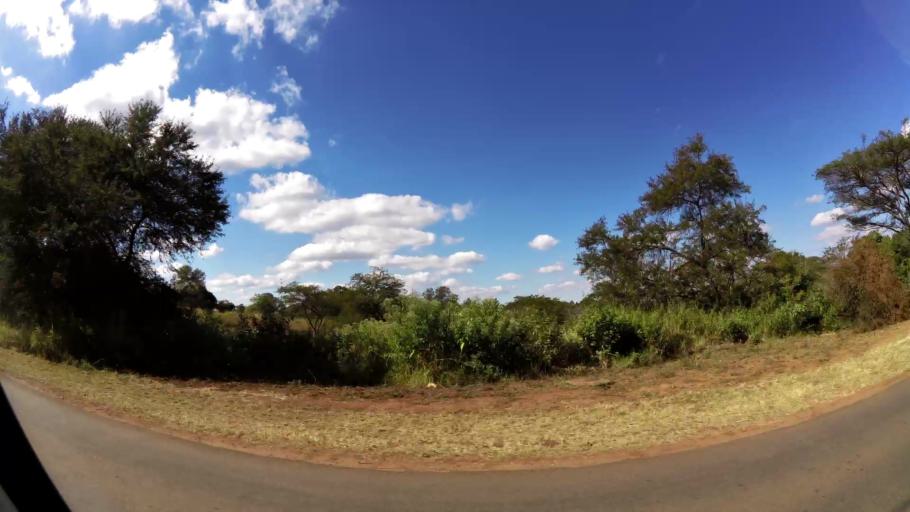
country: ZA
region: Limpopo
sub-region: Mopani District Municipality
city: Tzaneen
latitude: -23.8159
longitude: 30.1589
